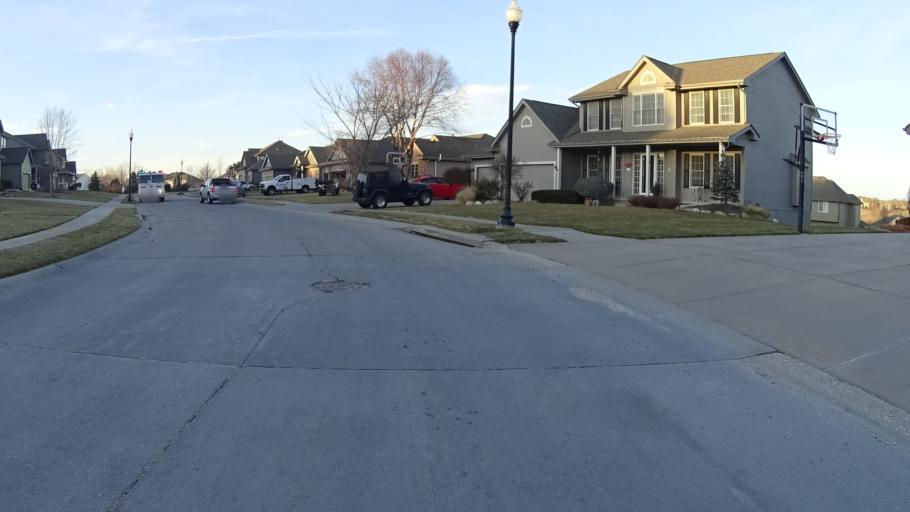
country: US
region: Nebraska
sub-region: Sarpy County
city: Papillion
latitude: 41.1309
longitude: -96.0672
